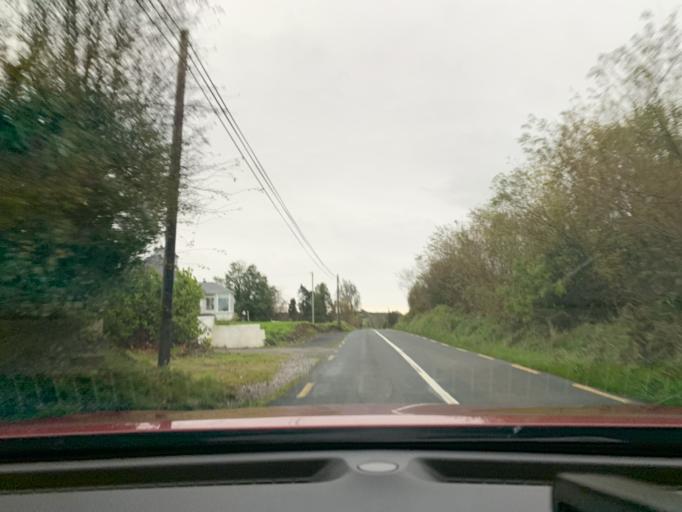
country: IE
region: Connaught
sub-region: Sligo
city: Ballymote
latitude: 54.0739
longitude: -8.5114
